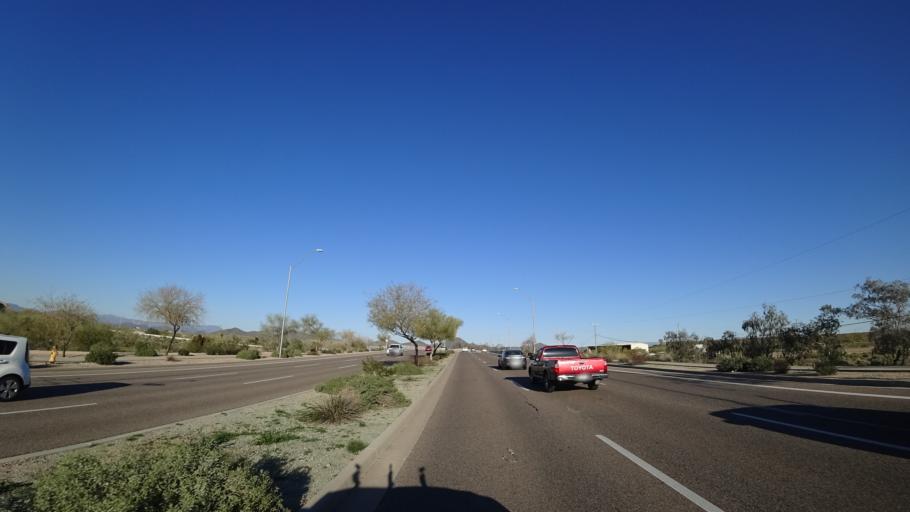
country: US
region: Arizona
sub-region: Maricopa County
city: Anthem
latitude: 33.7123
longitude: -112.1287
